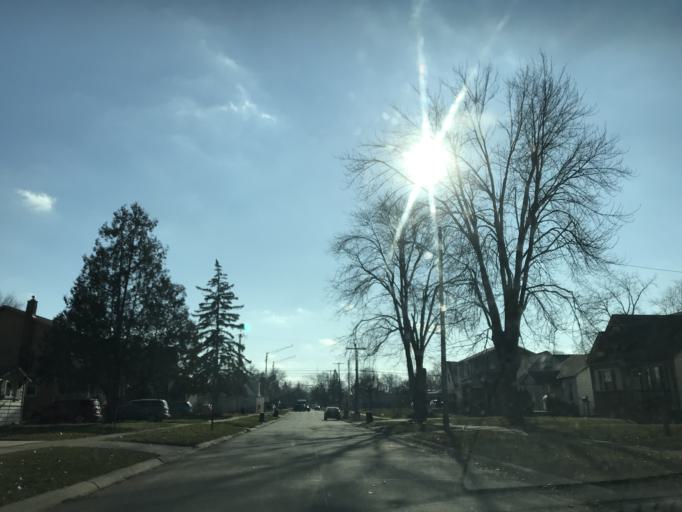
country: US
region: Michigan
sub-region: Oakland County
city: Madison Heights
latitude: 42.4919
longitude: -83.1136
